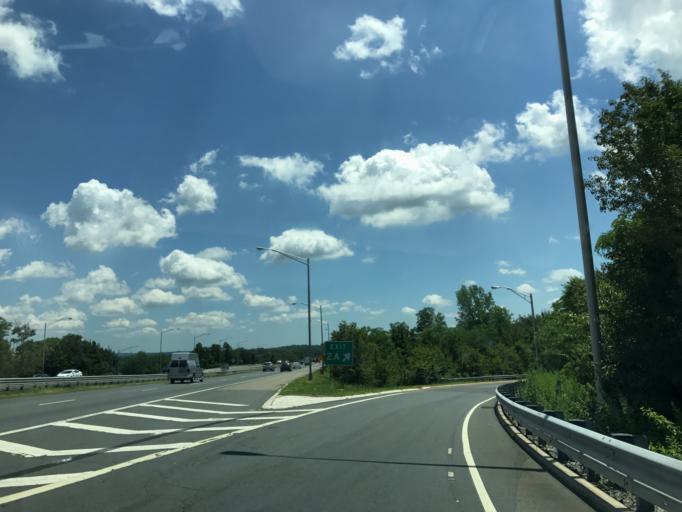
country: US
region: New Jersey
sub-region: Morris County
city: Madison
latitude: 40.7948
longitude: -74.4311
